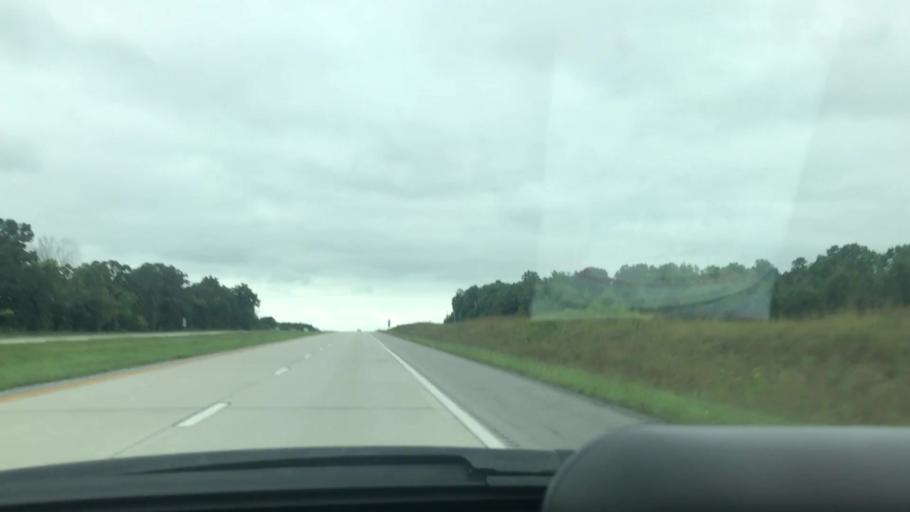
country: US
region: Missouri
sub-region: Greene County
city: Fair Grove
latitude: 37.4815
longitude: -93.1392
